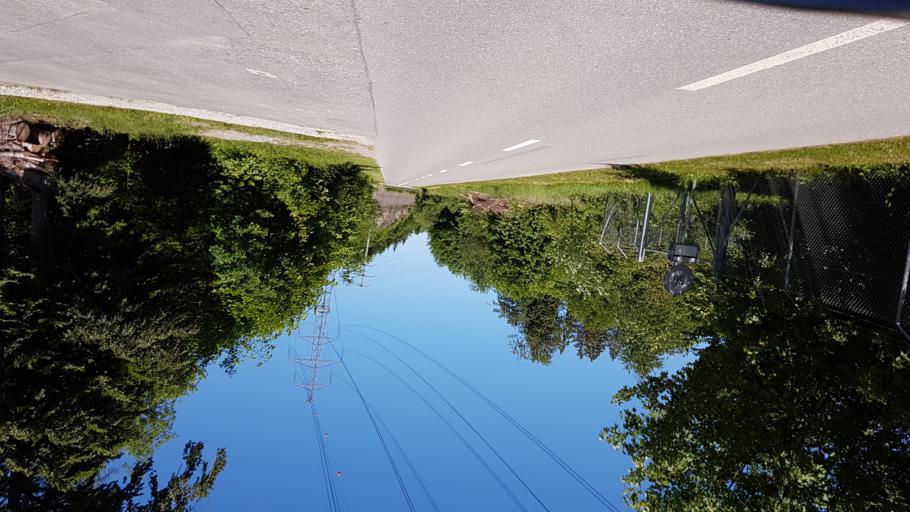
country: CH
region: Bern
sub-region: Frutigen-Niedersimmental District
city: Wimmis
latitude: 46.6937
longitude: 7.6471
